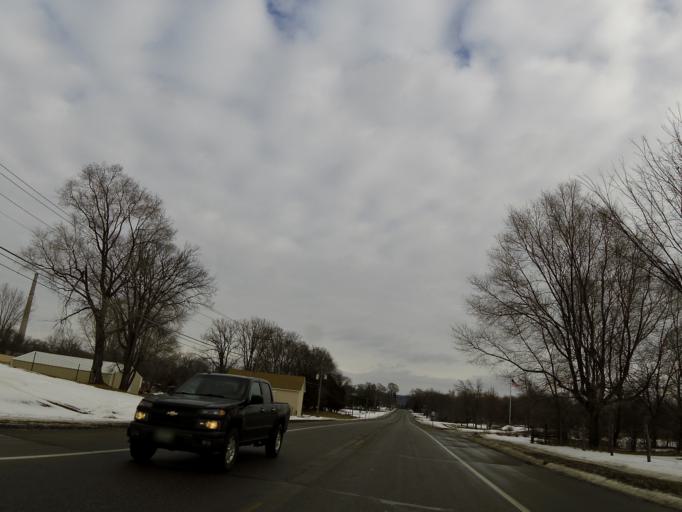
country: US
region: Minnesota
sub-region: Washington County
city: Oak Park Heights
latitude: 45.0215
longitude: -92.7923
